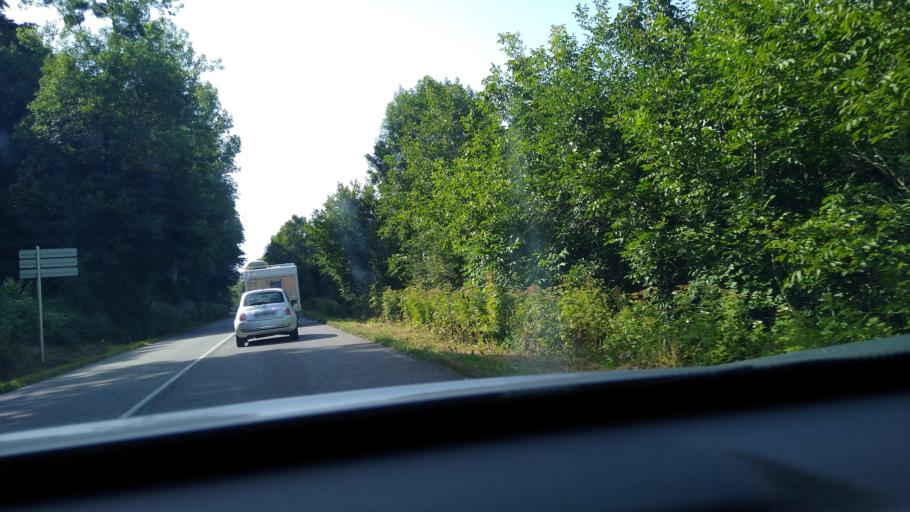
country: FR
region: Midi-Pyrenees
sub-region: Departement de l'Ariege
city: Saint-Lizier
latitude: 43.0320
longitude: 1.0816
